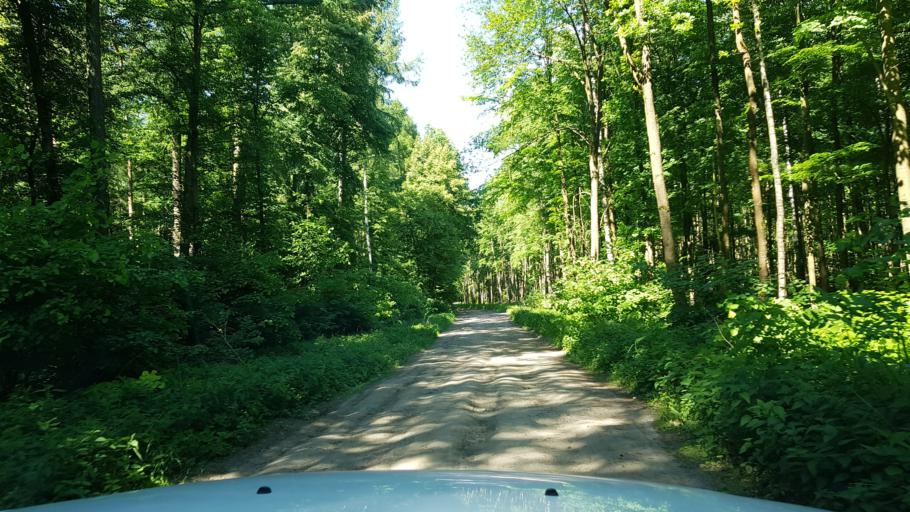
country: PL
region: West Pomeranian Voivodeship
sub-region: Powiat gryfinski
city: Banie
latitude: 53.1184
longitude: 14.5416
